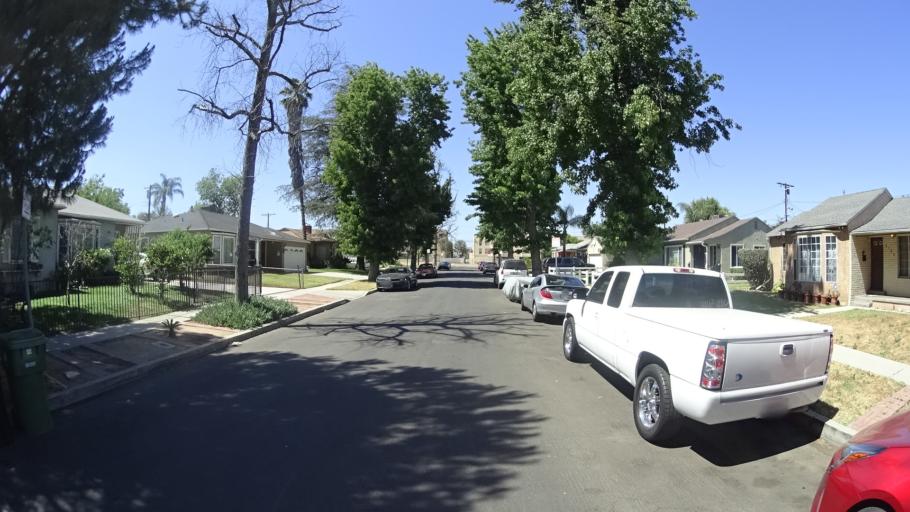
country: US
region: California
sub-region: Los Angeles County
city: Van Nuys
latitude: 34.1919
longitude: -118.4937
